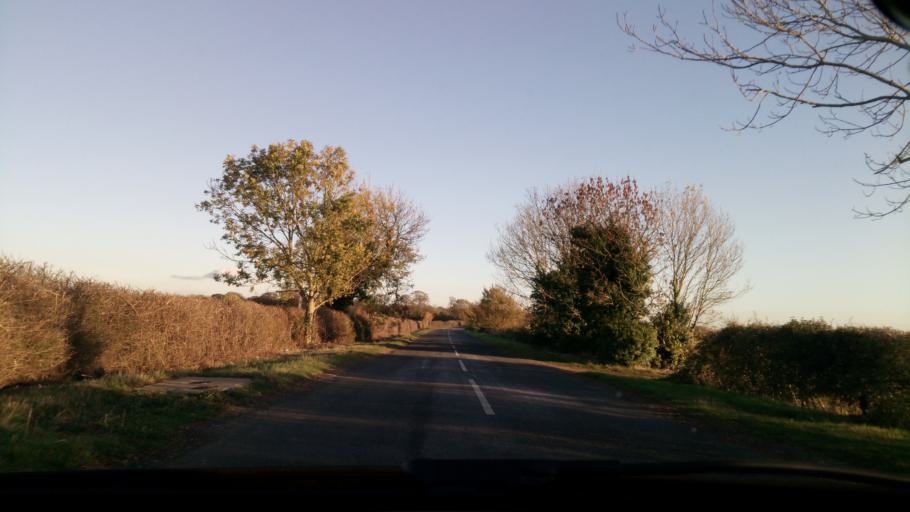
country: GB
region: England
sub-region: Peterborough
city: Barnack
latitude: 52.6273
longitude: -0.4249
